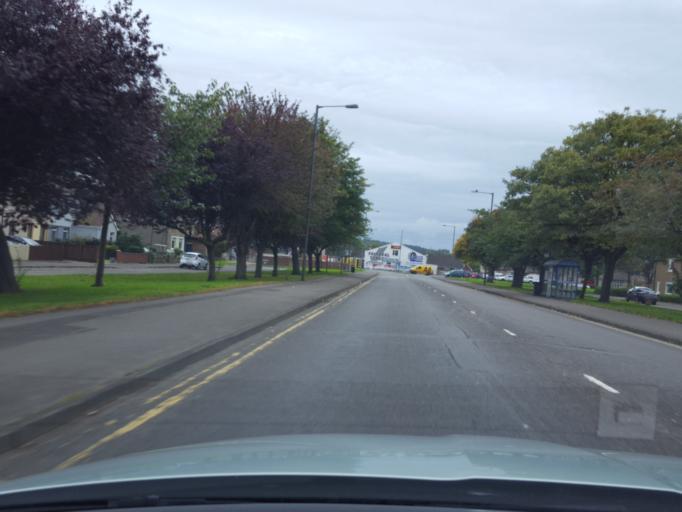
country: GB
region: Scotland
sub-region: Falkirk
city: Grangemouth
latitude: 56.0062
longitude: -3.7318
